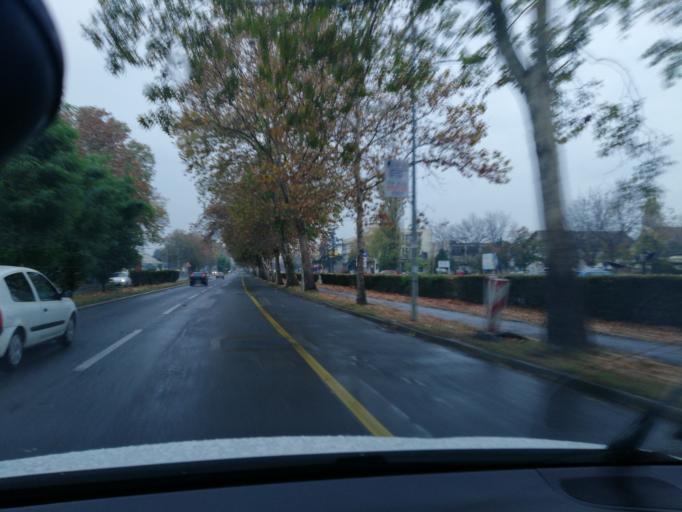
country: RS
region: Autonomna Pokrajina Vojvodina
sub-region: Juznobacki Okrug
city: Novi Sad
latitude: 45.2480
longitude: 19.8129
